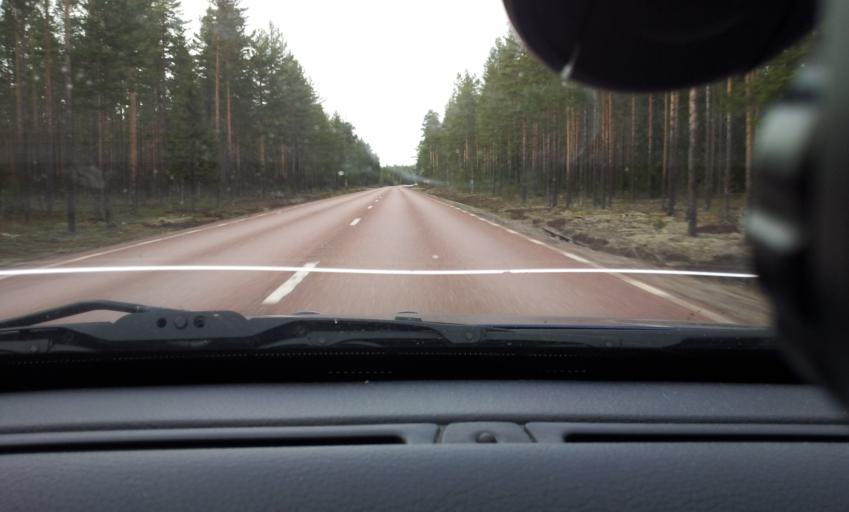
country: SE
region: Gaevleborg
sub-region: Ljusdals Kommun
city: Farila
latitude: 61.8261
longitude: 15.7547
